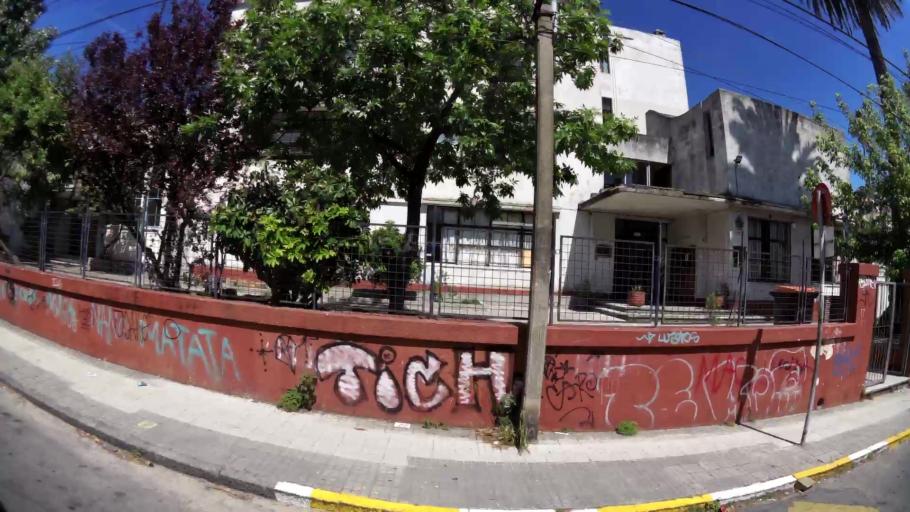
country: UY
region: Montevideo
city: Montevideo
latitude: -34.9159
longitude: -56.1608
